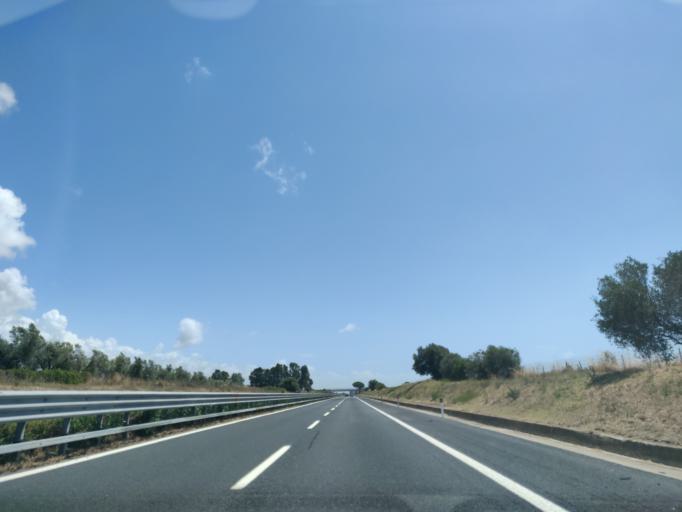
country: IT
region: Latium
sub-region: Citta metropolitana di Roma Capitale
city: Marina San Nicola
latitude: 41.9589
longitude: 12.1249
